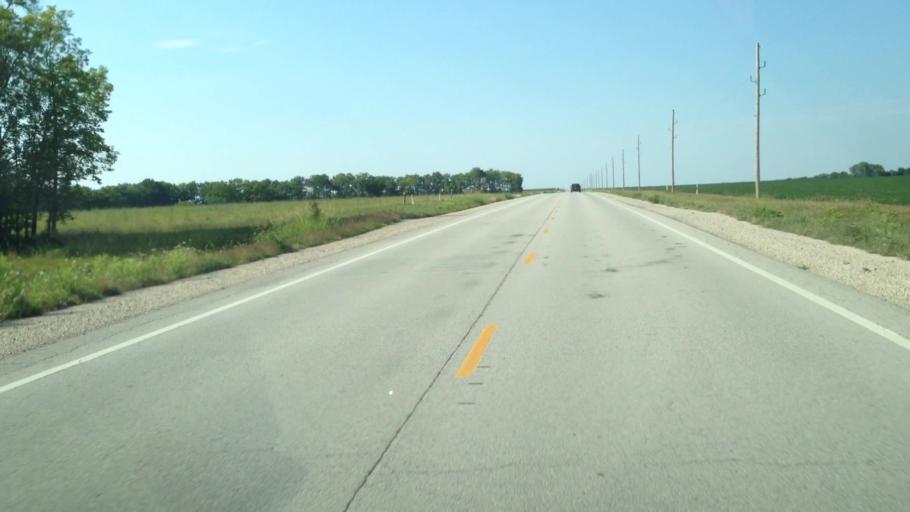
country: US
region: Kansas
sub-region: Anderson County
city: Garnett
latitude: 38.0430
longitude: -95.1697
